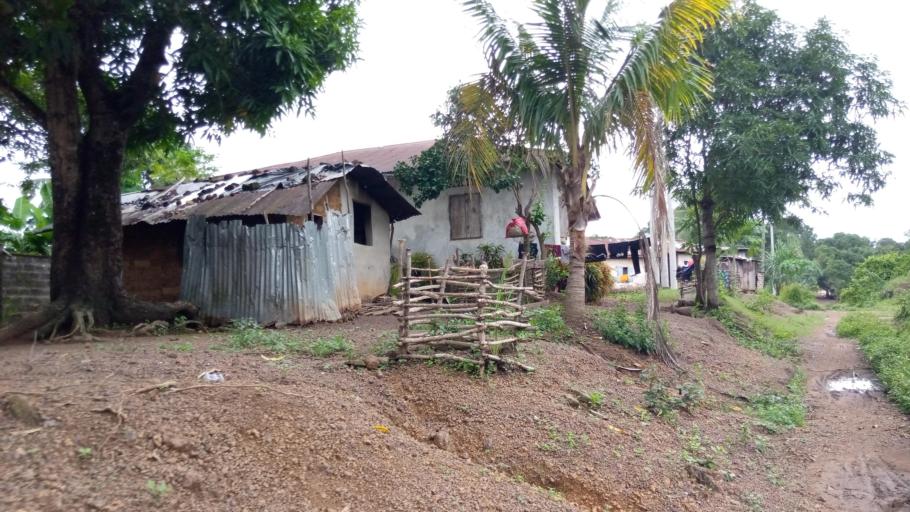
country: SL
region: Southern Province
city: Moyamba
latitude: 8.1590
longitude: -12.4343
